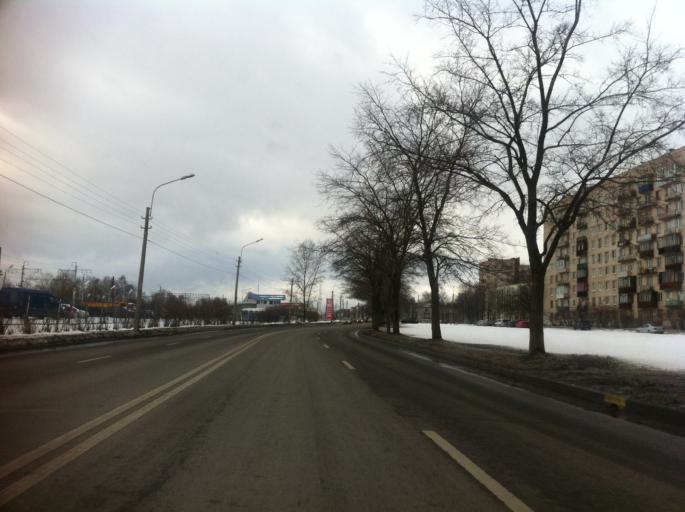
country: RU
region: St.-Petersburg
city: Sosnovaya Polyana
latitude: 59.8250
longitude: 30.1532
